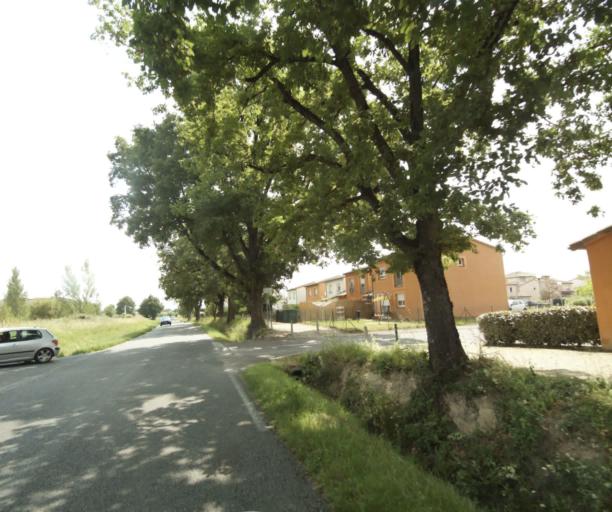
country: FR
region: Midi-Pyrenees
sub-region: Departement du Tarn-et-Garonne
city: Montauban
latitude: 44.0409
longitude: 1.3751
